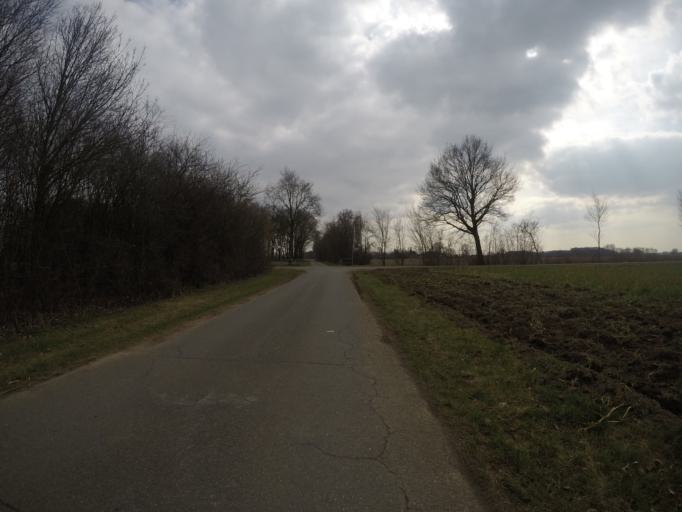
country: DE
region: North Rhine-Westphalia
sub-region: Regierungsbezirk Dusseldorf
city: Bocholt
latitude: 51.7972
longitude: 6.5686
